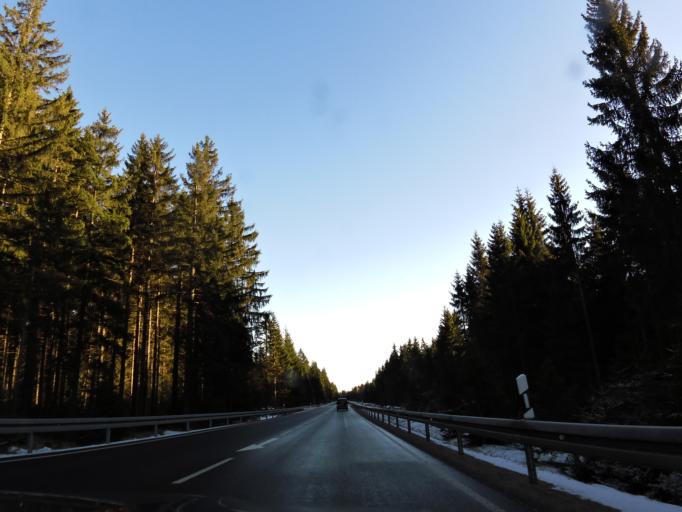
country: DE
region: Bavaria
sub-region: Upper Franconia
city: Fichtelberg
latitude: 50.0267
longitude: 11.8589
